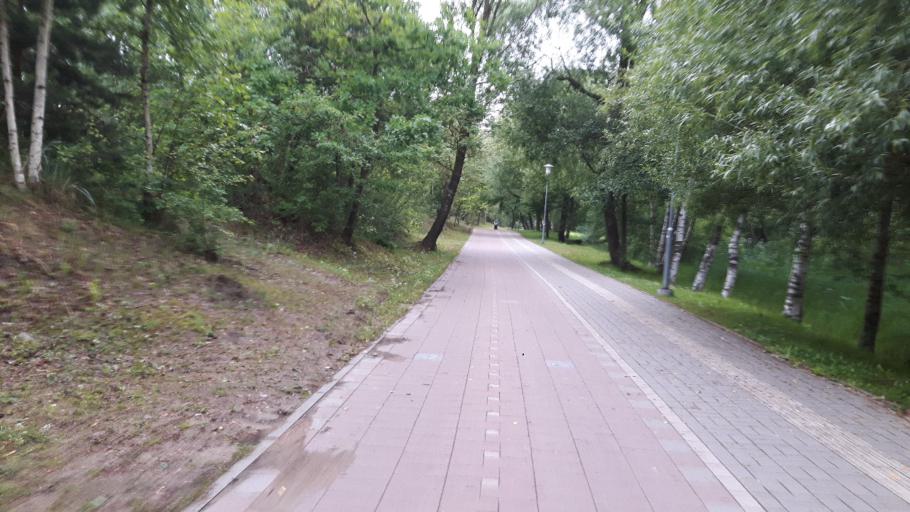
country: LV
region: Liepaja
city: Liepaja
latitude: 56.4978
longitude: 20.9960
